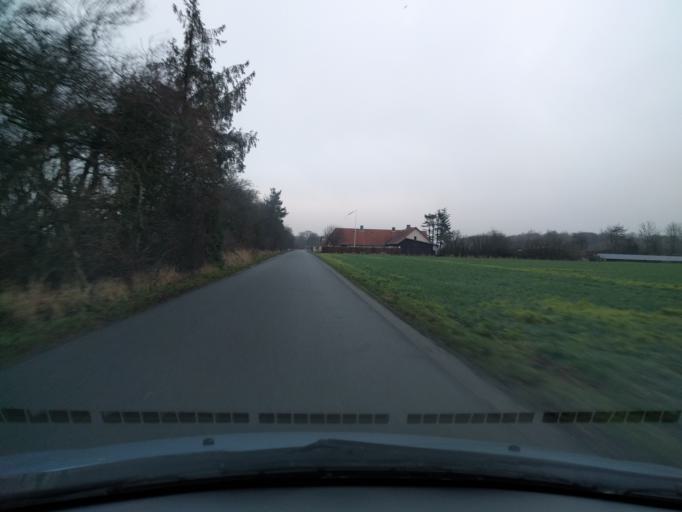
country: DK
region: South Denmark
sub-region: Odense Kommune
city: Bullerup
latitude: 55.4156
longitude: 10.5200
